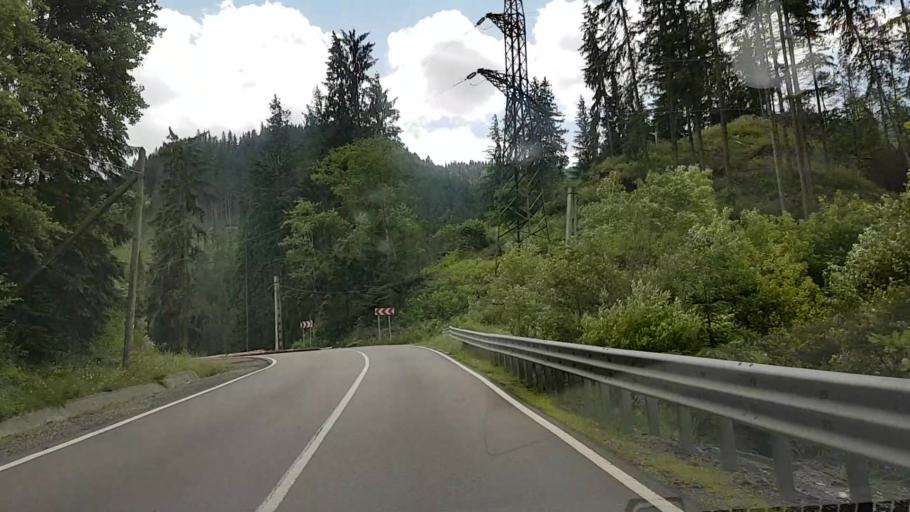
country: RO
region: Suceava
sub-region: Comuna Crucea
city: Crucea
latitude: 47.3627
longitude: 25.5919
